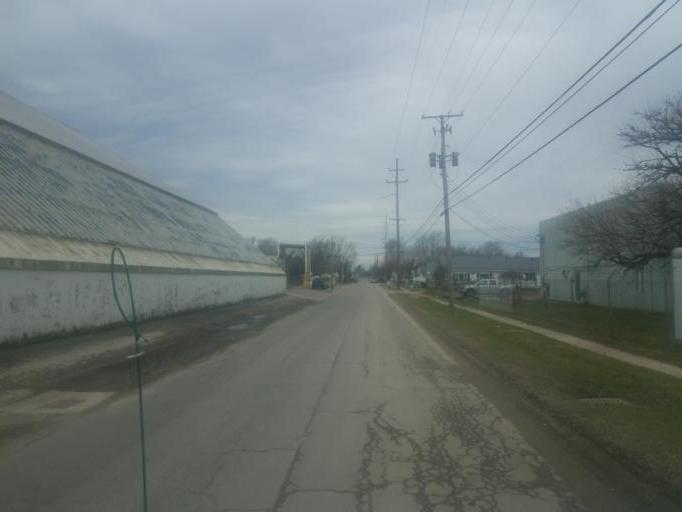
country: US
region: Ohio
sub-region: Marion County
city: Marion
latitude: 40.5952
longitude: -83.1111
